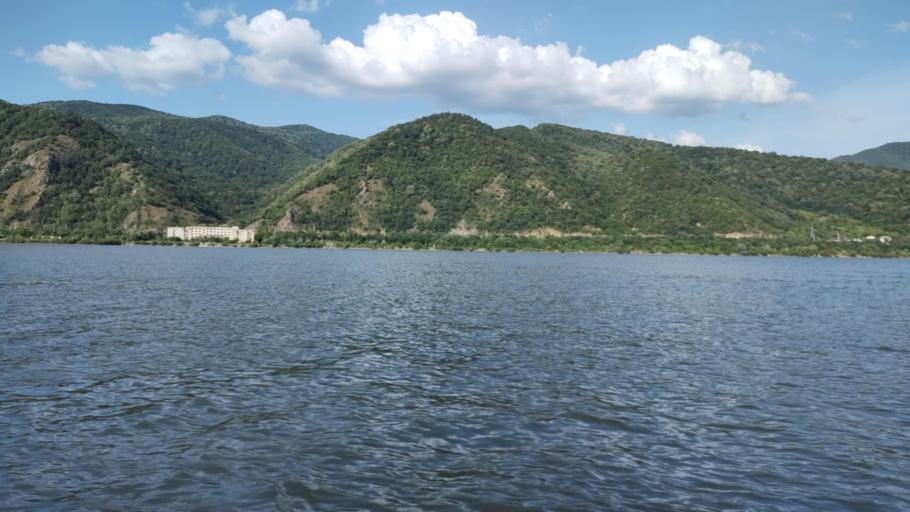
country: RO
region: Caras-Severin
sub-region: Comuna Berzasca
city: Berzasca
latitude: 44.6254
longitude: 21.9961
